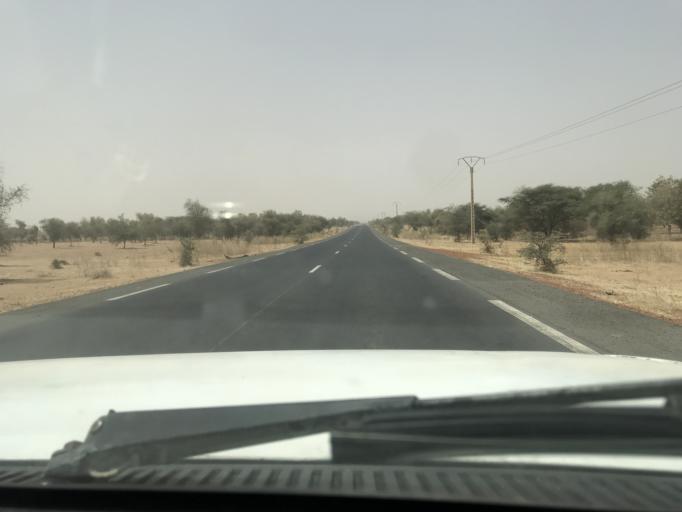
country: SN
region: Louga
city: Ndibene Dahra
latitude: 15.3441
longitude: -15.3980
